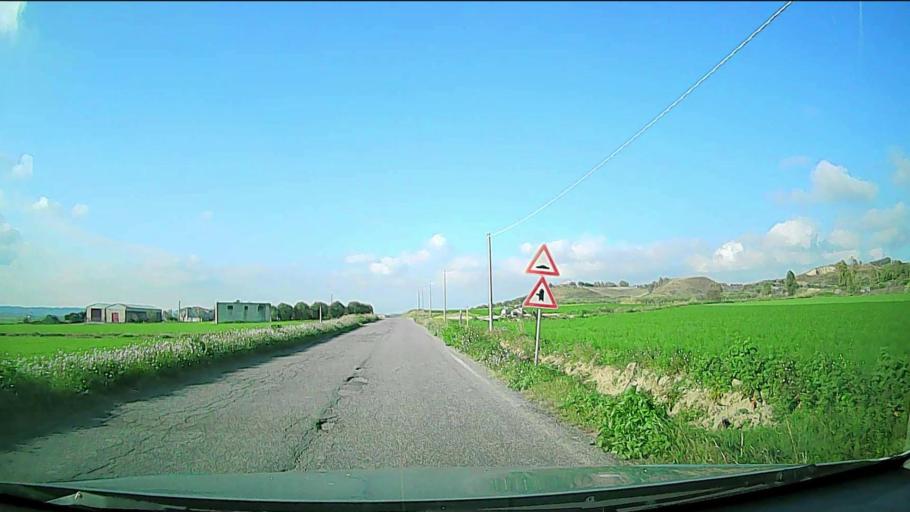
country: IT
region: Calabria
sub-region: Provincia di Crotone
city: Tronca
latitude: 39.2022
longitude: 17.0942
